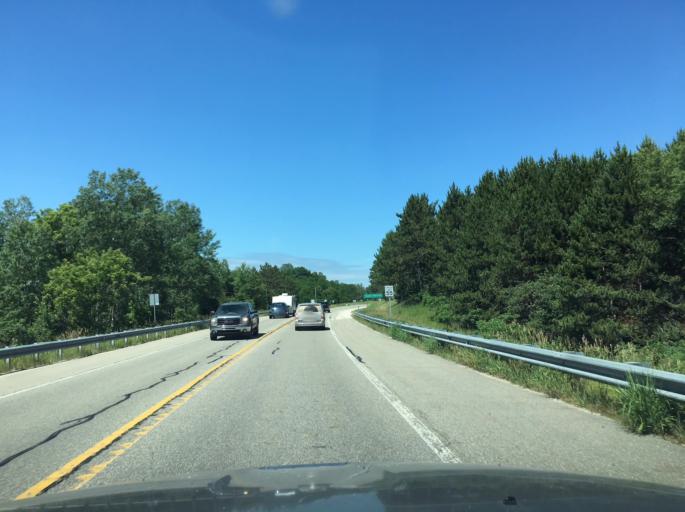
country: US
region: Michigan
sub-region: Osceola County
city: Reed City
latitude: 43.8879
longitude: -85.6387
